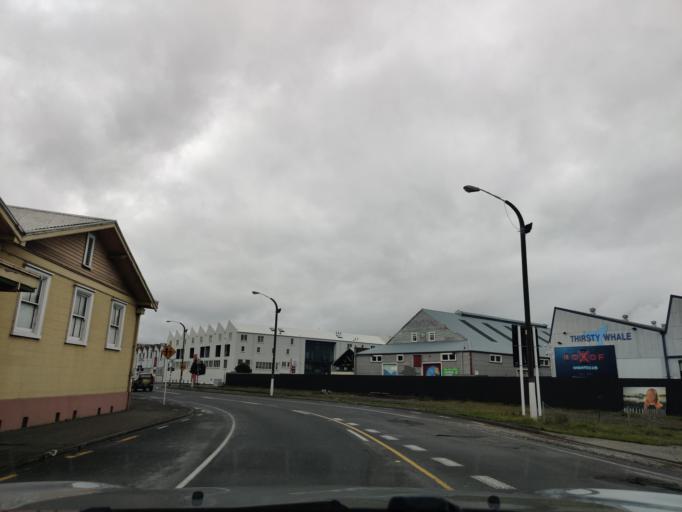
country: NZ
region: Hawke's Bay
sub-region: Napier City
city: Napier
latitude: -39.4830
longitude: 176.8956
